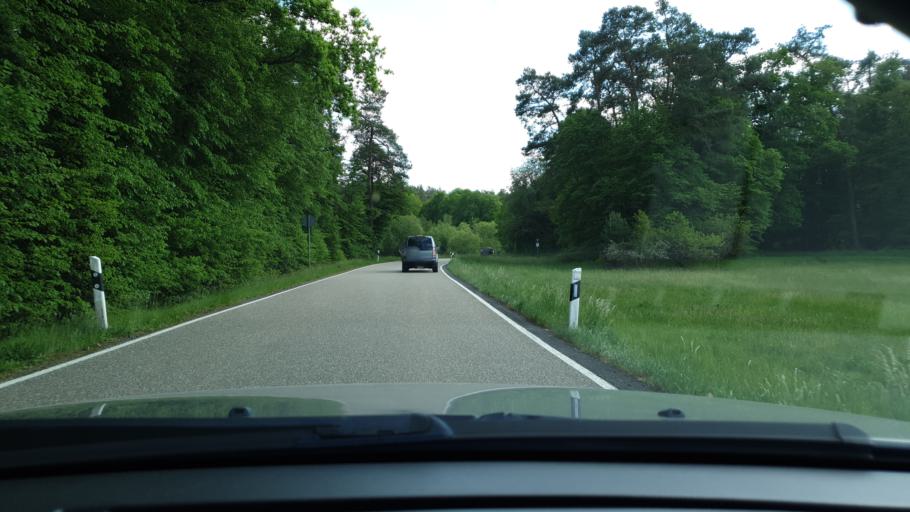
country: DE
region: Rheinland-Pfalz
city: Rodenbach
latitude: 49.4660
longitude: 7.6392
